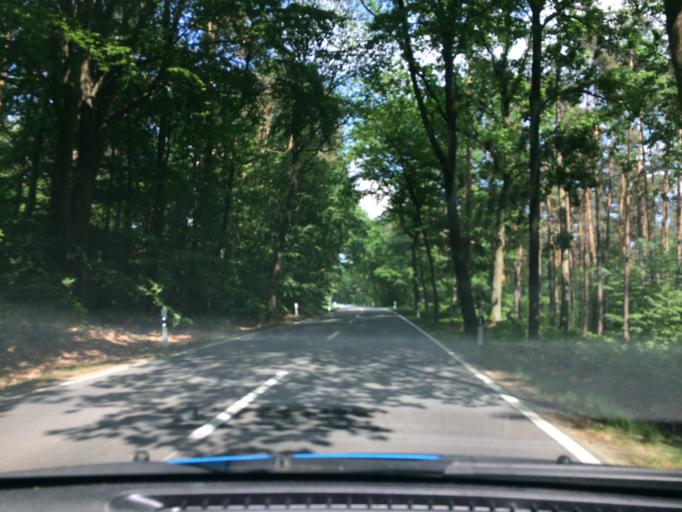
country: DE
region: Lower Saxony
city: Neu Darchau
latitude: 53.2182
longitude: 10.8546
